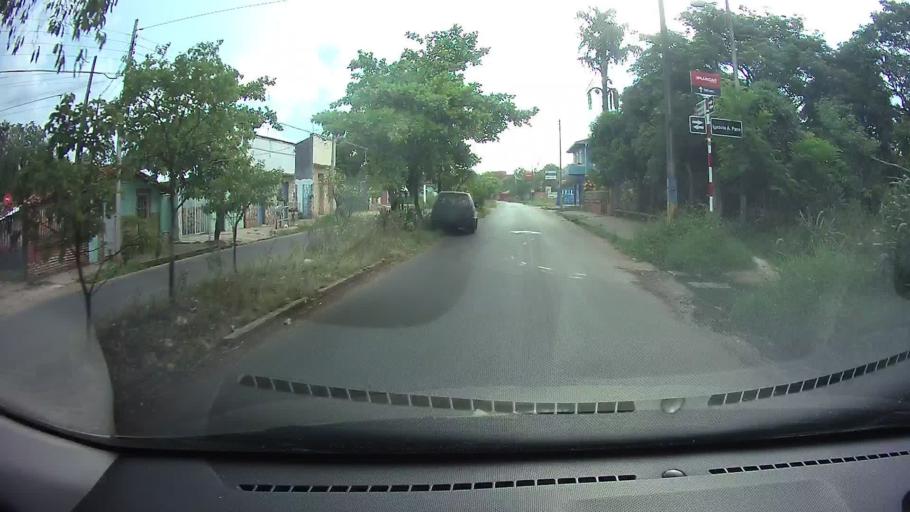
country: PY
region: Central
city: San Lorenzo
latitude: -25.2712
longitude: -57.4806
